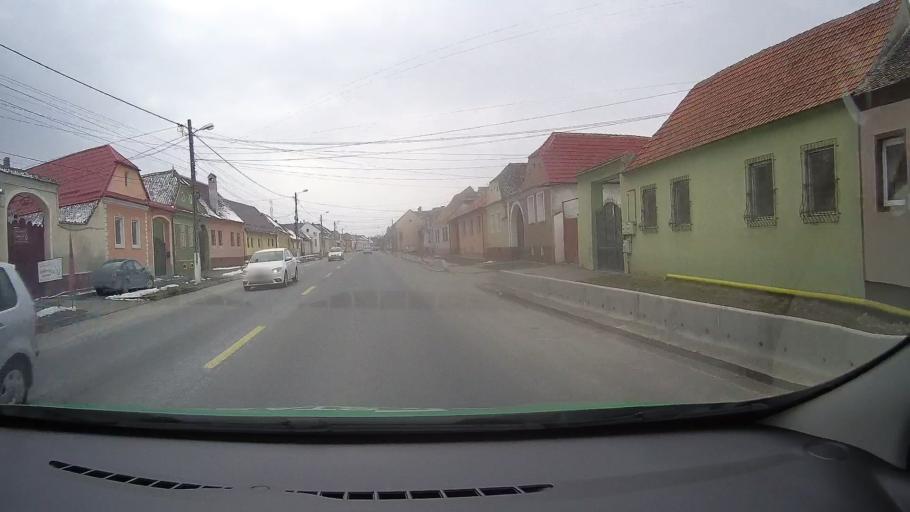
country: RO
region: Brasov
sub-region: Comuna Cristian
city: Cristian
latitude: 45.6219
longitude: 25.4795
